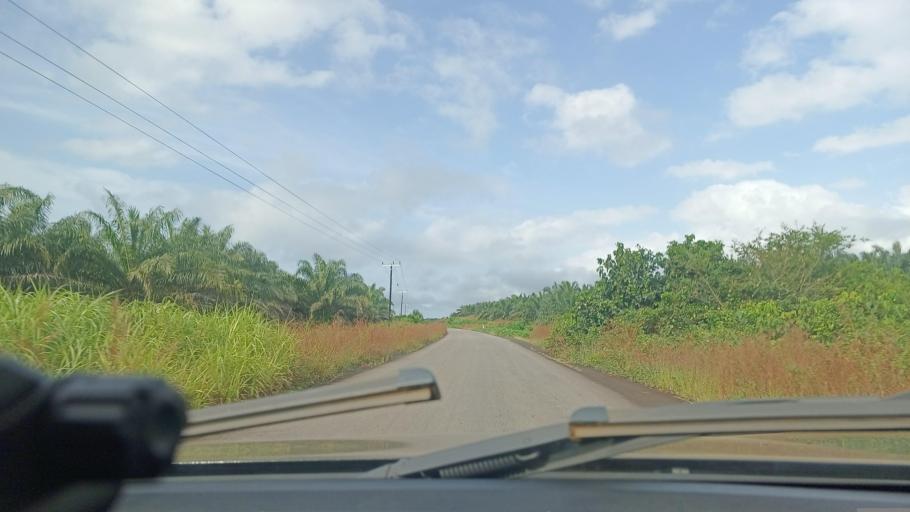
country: LR
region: Bomi
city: Tubmanburg
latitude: 6.7262
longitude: -11.0451
